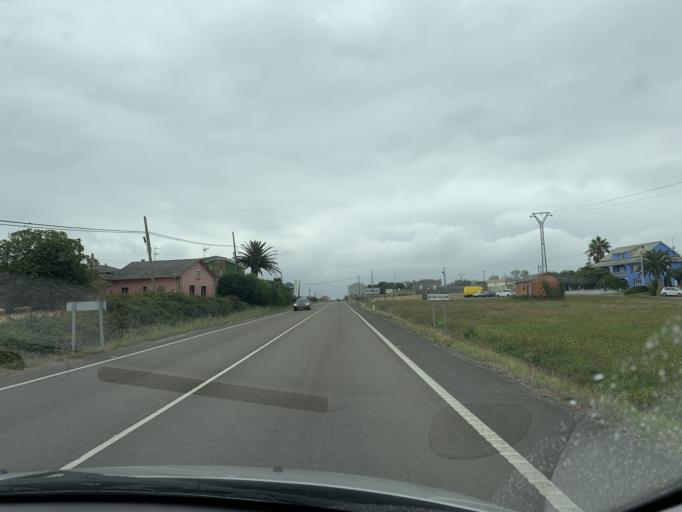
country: ES
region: Galicia
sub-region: Provincia de Lugo
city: Ribadeo
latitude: 43.5466
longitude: -7.1061
